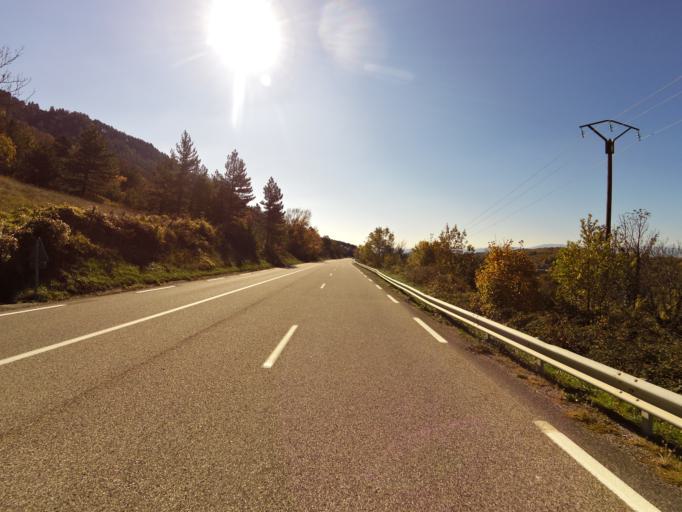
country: FR
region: Rhone-Alpes
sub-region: Departement de l'Ardeche
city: Vesseaux
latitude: 44.6912
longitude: 4.4721
